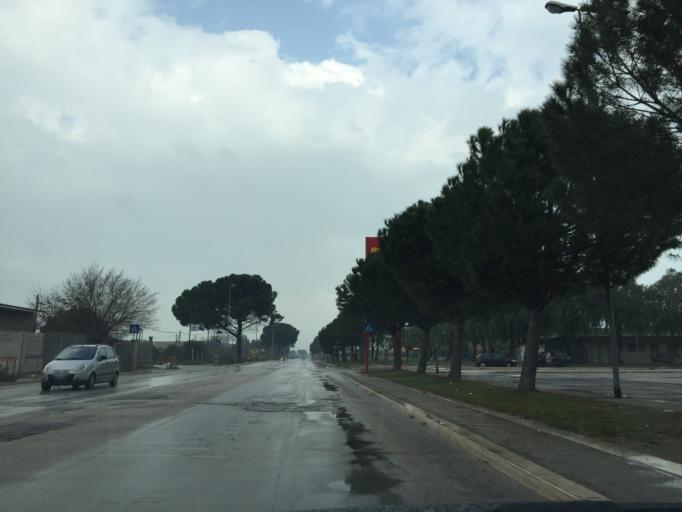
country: IT
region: Apulia
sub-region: Provincia di Foggia
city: Foggia
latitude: 41.4743
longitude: 15.5359
